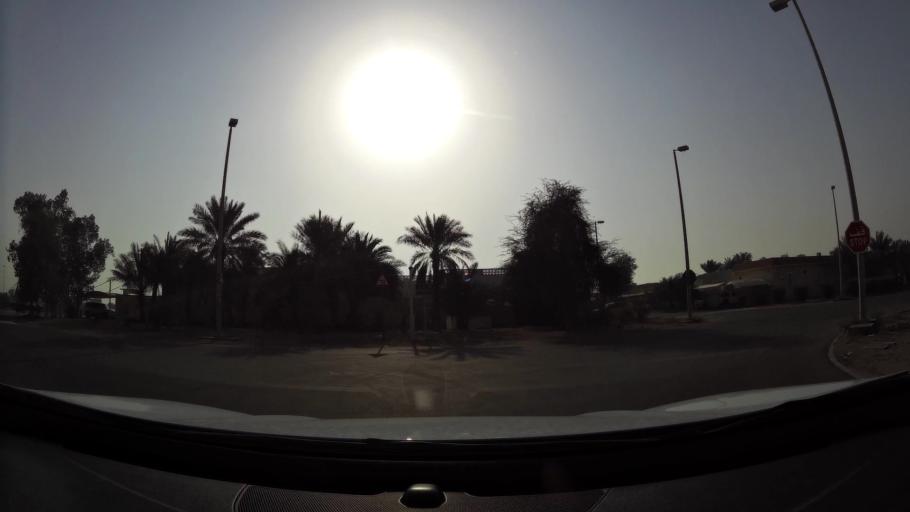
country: AE
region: Abu Dhabi
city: Abu Dhabi
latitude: 24.2697
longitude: 54.6600
